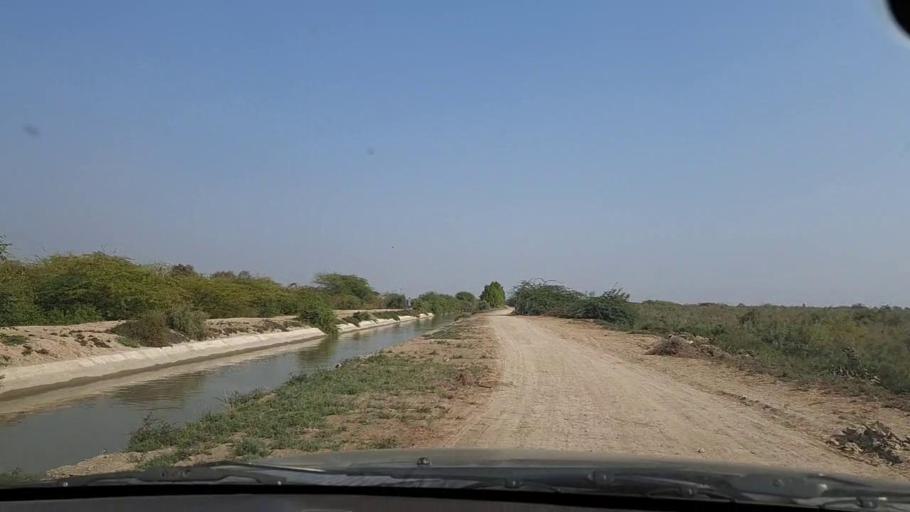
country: PK
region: Sindh
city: Mirpur Sakro
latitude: 24.3419
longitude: 67.7085
